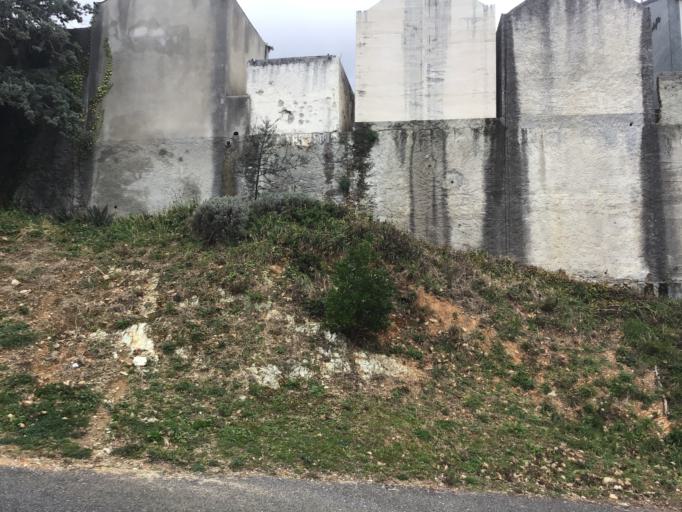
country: IT
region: Liguria
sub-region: Provincia di Savona
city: Orco Feglino
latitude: 44.2237
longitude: 8.3264
